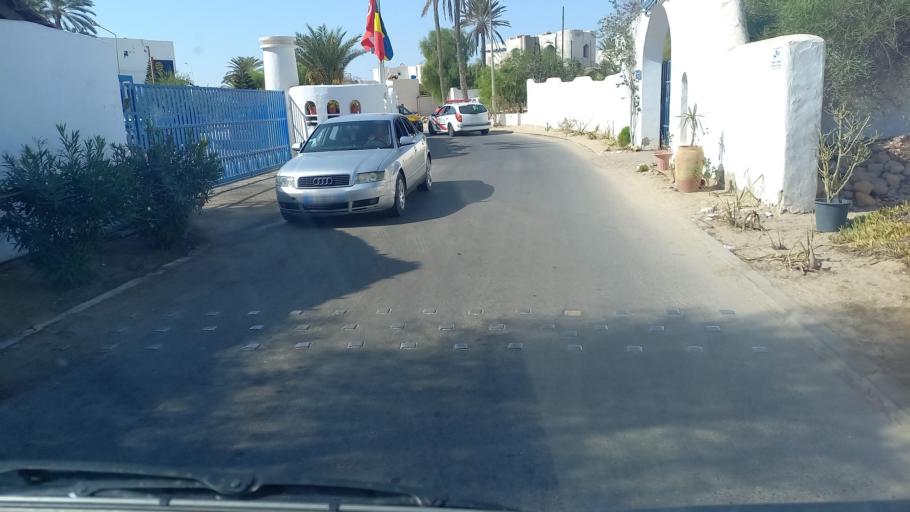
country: TN
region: Madanin
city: Midoun
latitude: 33.8498
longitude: 10.9883
